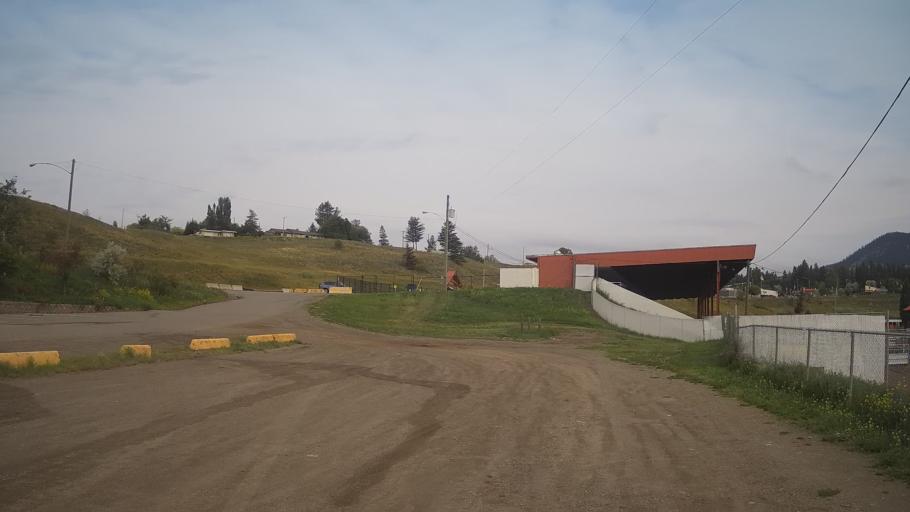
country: CA
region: British Columbia
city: Williams Lake
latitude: 52.1241
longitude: -122.1322
